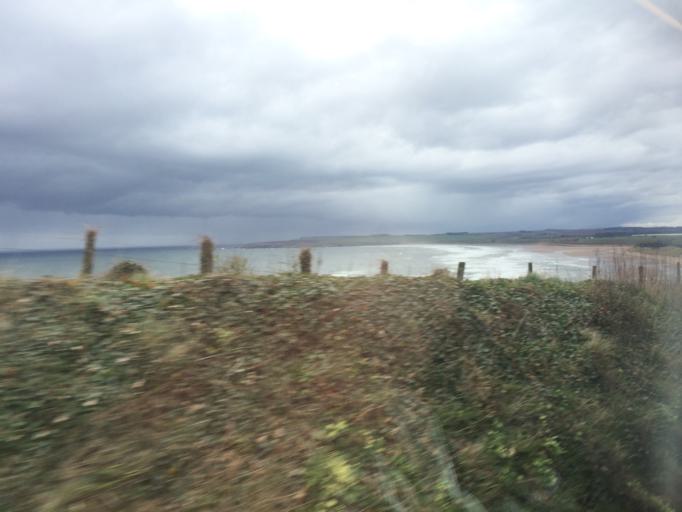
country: GB
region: Scotland
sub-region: Angus
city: Montrose
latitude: 56.6673
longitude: -2.4919
